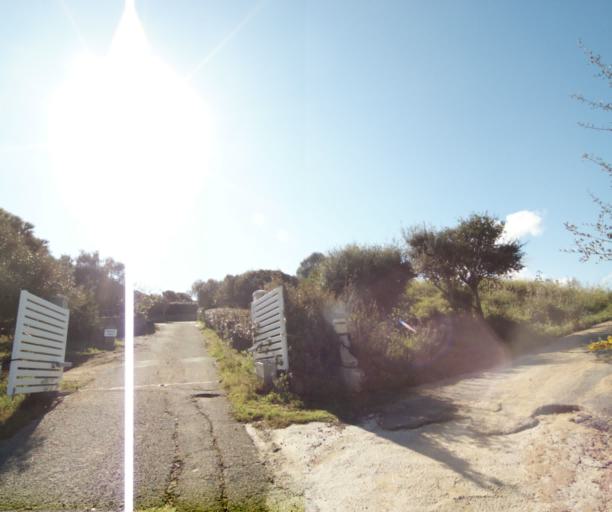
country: FR
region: Corsica
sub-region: Departement de la Corse-du-Sud
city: Propriano
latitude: 41.6680
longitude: 8.9013
